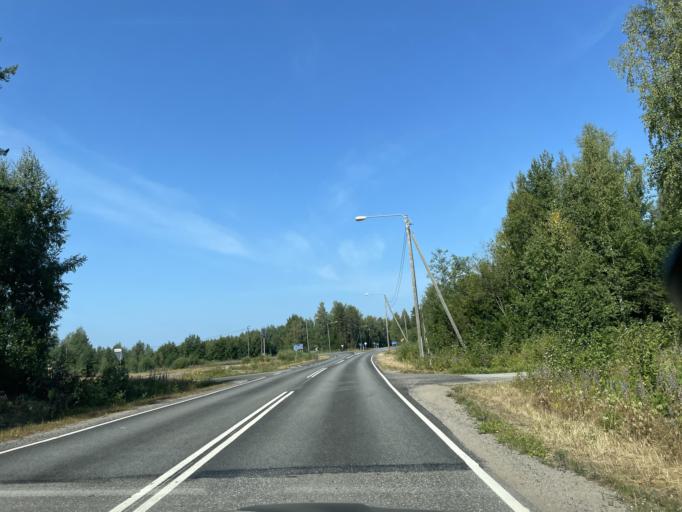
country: FI
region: Central Finland
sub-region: Saarijaervi-Viitasaari
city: Pihtipudas
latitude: 63.3761
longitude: 25.5933
